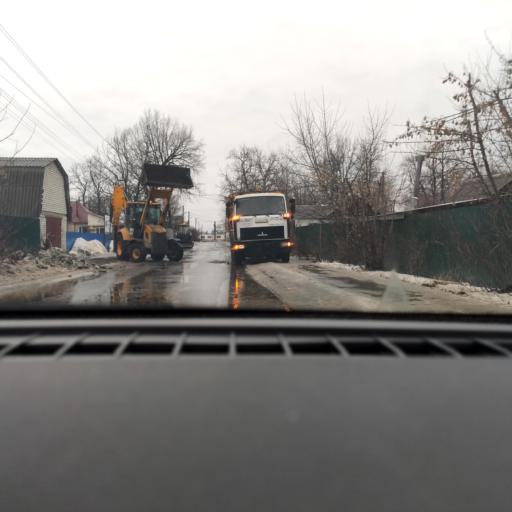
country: RU
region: Voronezj
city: Somovo
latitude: 51.7364
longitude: 39.3566
